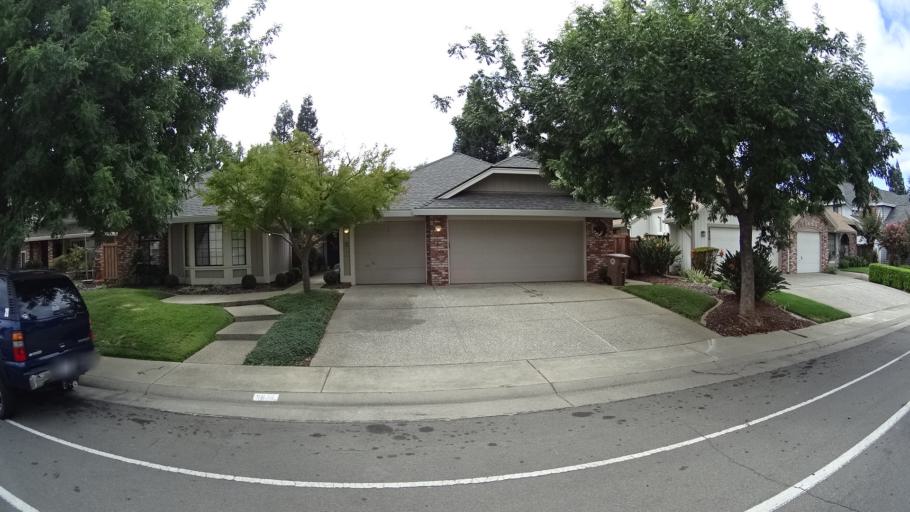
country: US
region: California
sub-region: Sacramento County
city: Laguna
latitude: 38.4185
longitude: -121.4369
